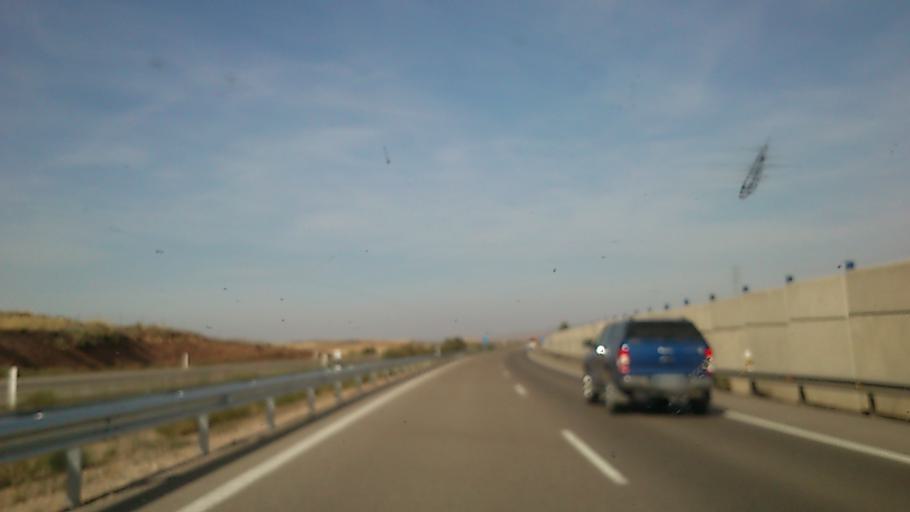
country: ES
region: Aragon
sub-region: Provincia de Zaragoza
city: Muel
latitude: 41.4486
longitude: -1.1348
